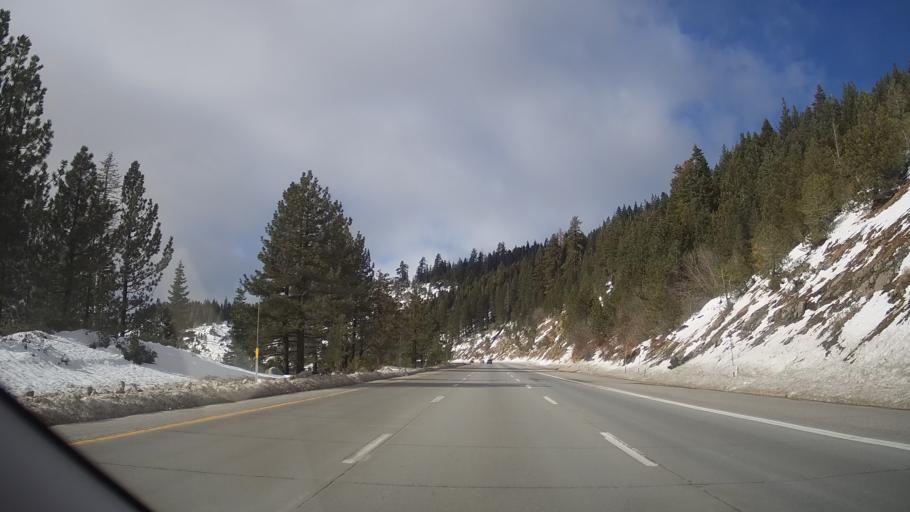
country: US
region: California
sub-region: Nevada County
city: Truckee
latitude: 39.3393
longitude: -120.3087
